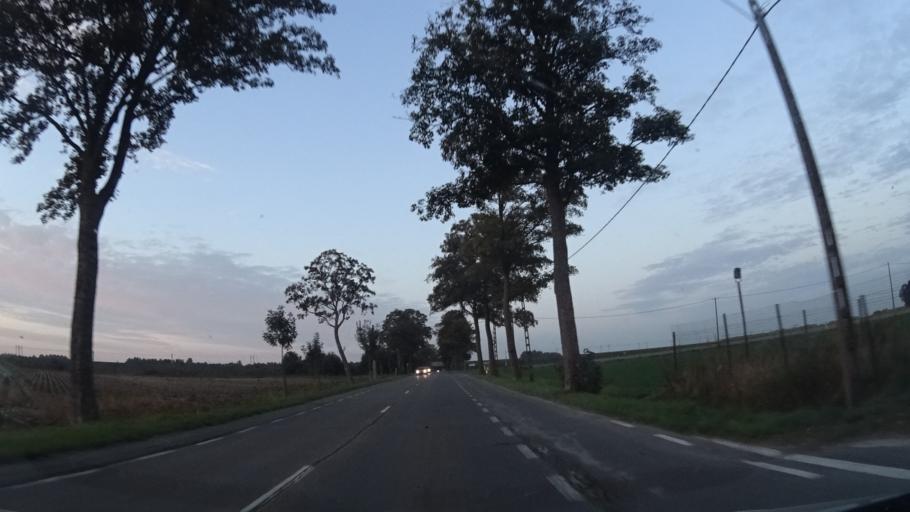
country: BE
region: Wallonia
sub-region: Province du Hainaut
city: Peruwelz
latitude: 50.5629
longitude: 3.6124
